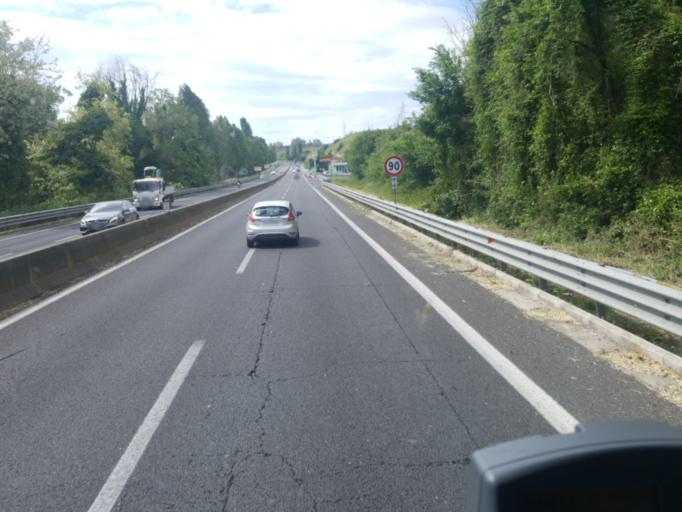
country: IT
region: Latium
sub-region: Citta metropolitana di Roma Capitale
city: Valle Santa
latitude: 41.8908
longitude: 12.2980
